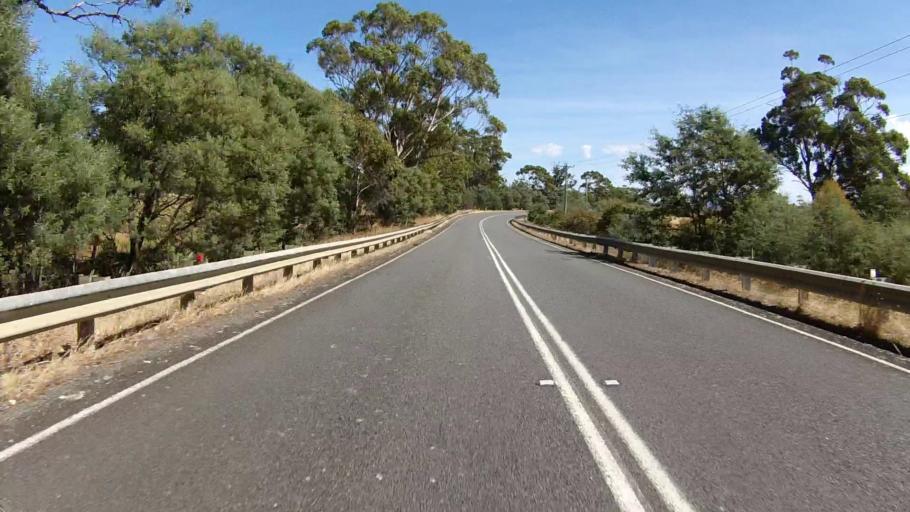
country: AU
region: Tasmania
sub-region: Sorell
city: Sorell
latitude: -42.5900
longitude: 147.7984
